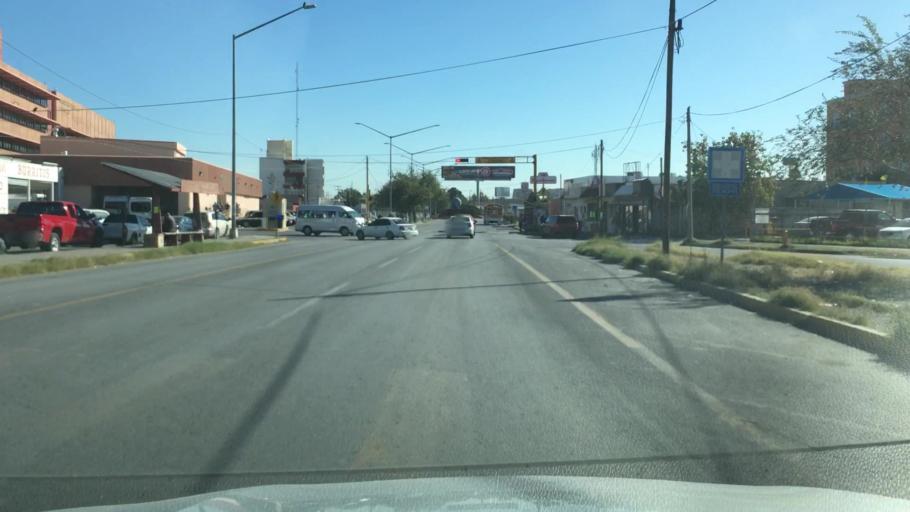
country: MX
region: Chihuahua
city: Ciudad Juarez
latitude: 31.7391
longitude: -106.4520
